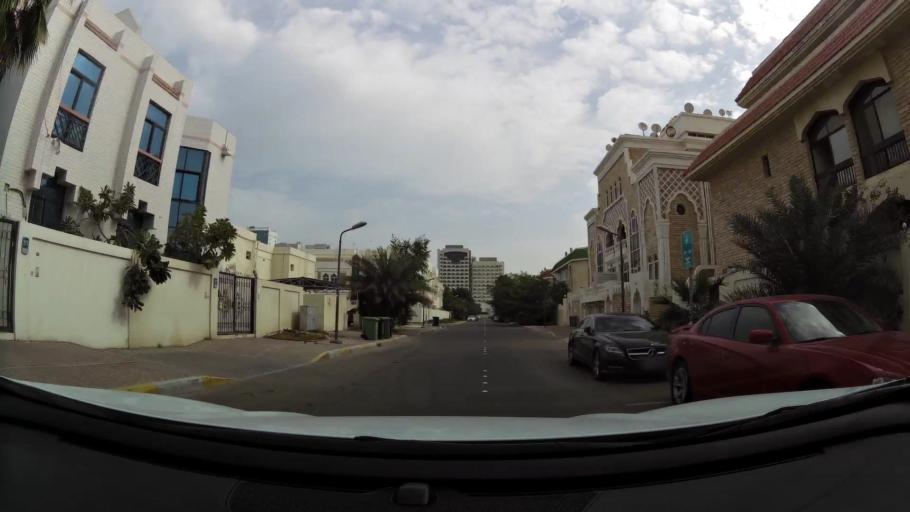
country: AE
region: Abu Dhabi
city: Abu Dhabi
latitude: 24.4557
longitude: 54.3786
